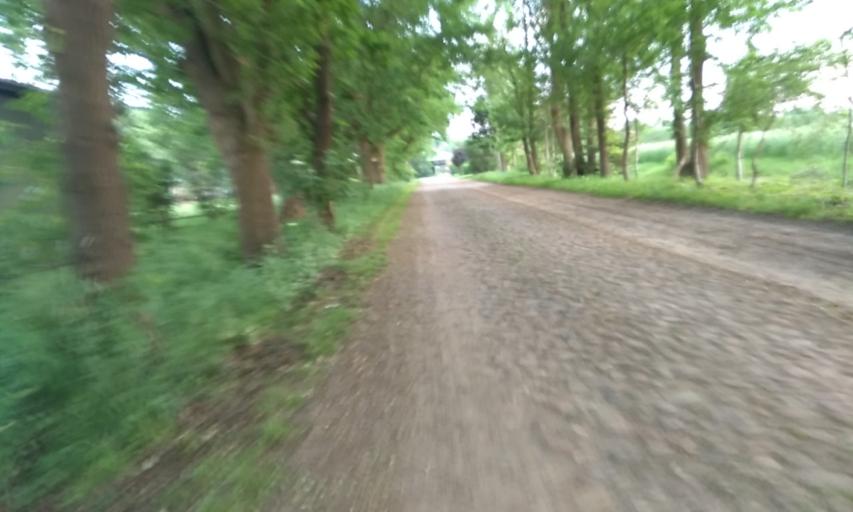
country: DE
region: Lower Saxony
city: Deinste
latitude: 53.5274
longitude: 9.4797
